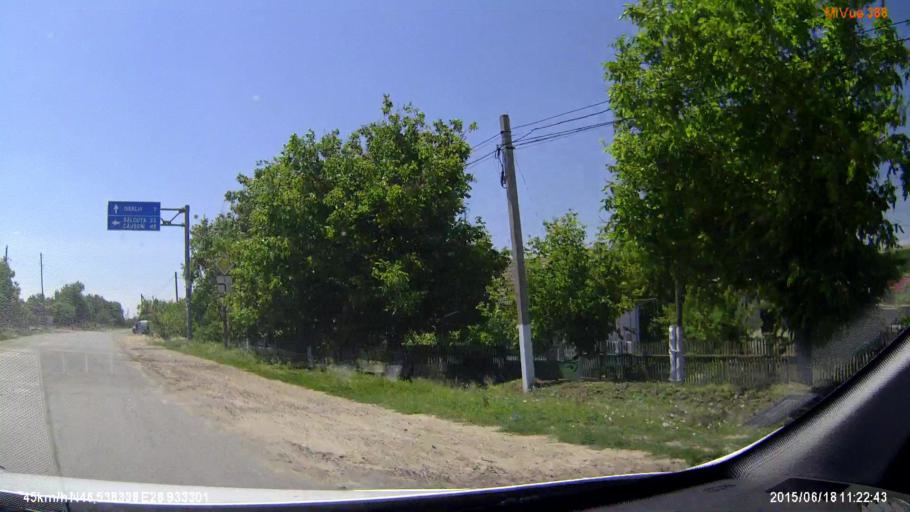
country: MD
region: Cimislia
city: Cimislia
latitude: 46.5386
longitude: 28.9333
